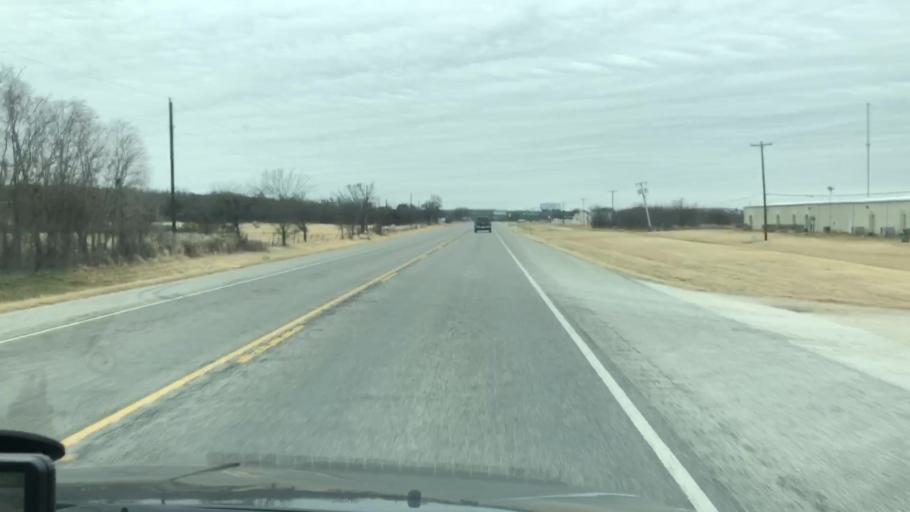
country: US
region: Texas
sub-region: Palo Pinto County
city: Mineral Wells
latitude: 32.8491
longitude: -98.0983
